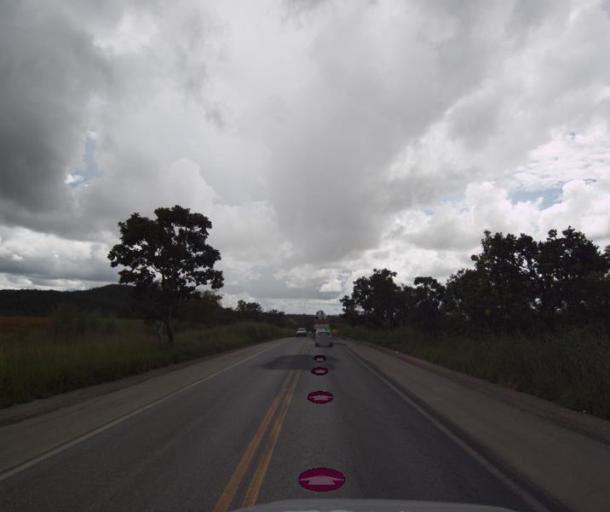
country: BR
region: Goias
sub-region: Uruacu
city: Uruacu
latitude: -14.2331
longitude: -49.1346
